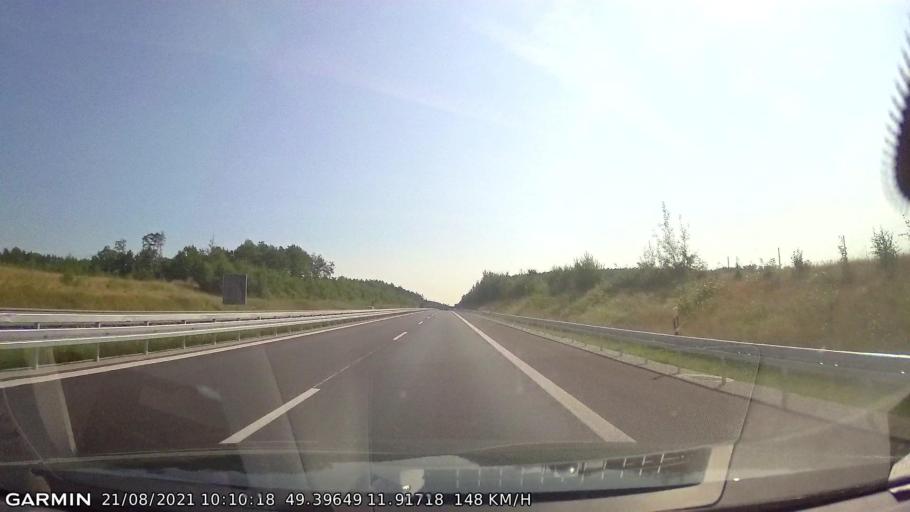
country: DE
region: Bavaria
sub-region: Upper Palatinate
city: Ebermannsdorf
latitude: 49.3965
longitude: 11.9173
